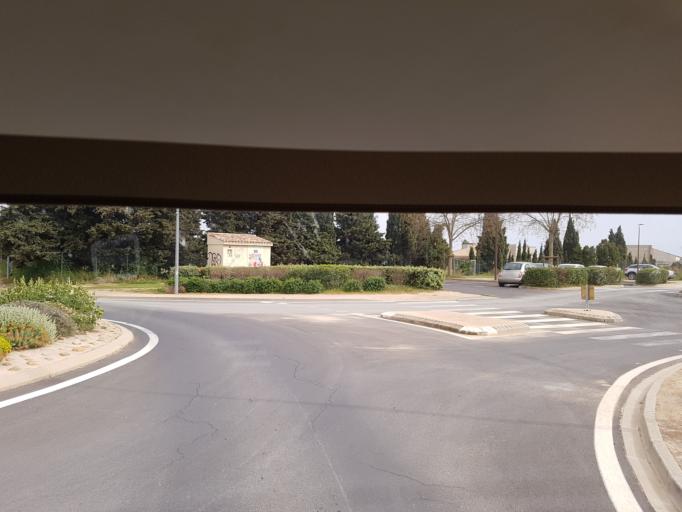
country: FR
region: Languedoc-Roussillon
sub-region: Departement de l'Herault
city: Vendres
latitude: 43.2700
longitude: 3.2169
